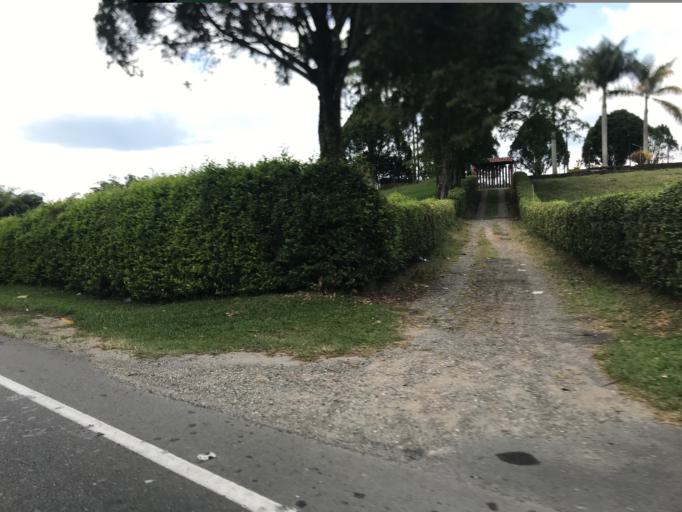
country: CO
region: Quindio
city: Armenia
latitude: 4.4972
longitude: -75.6804
